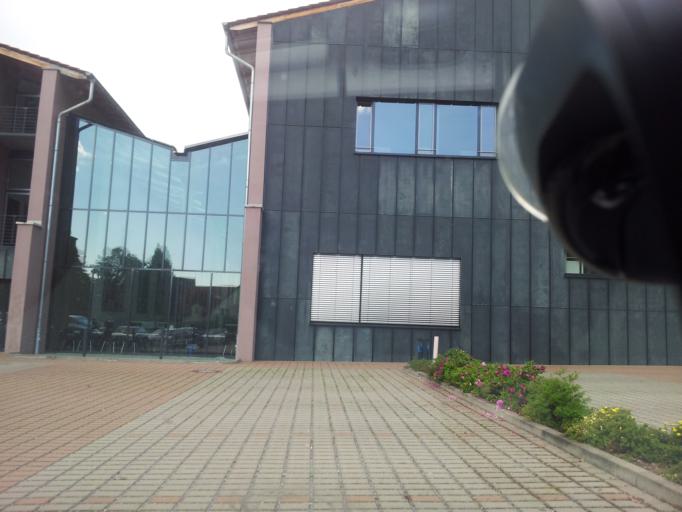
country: DE
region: Saxony-Anhalt
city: Wernigerode
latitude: 51.8277
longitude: 10.7604
